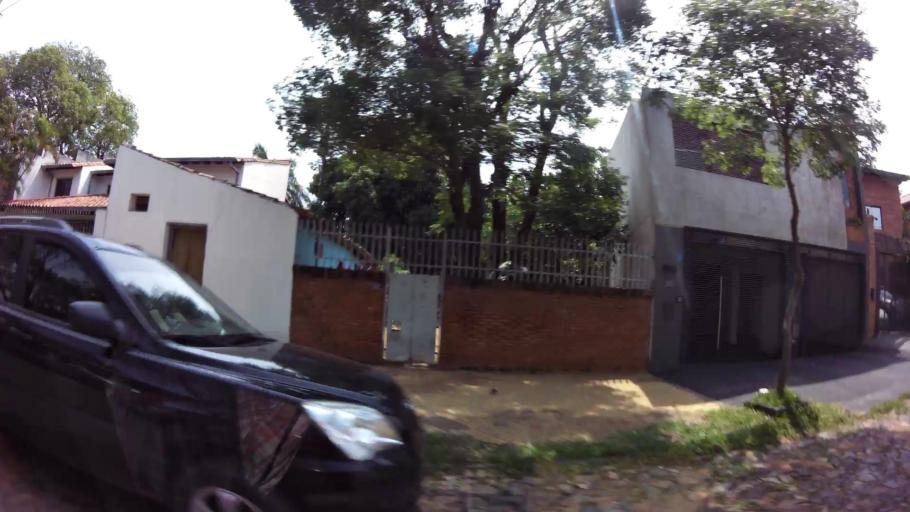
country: PY
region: Asuncion
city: Asuncion
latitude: -25.2813
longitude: -57.5962
